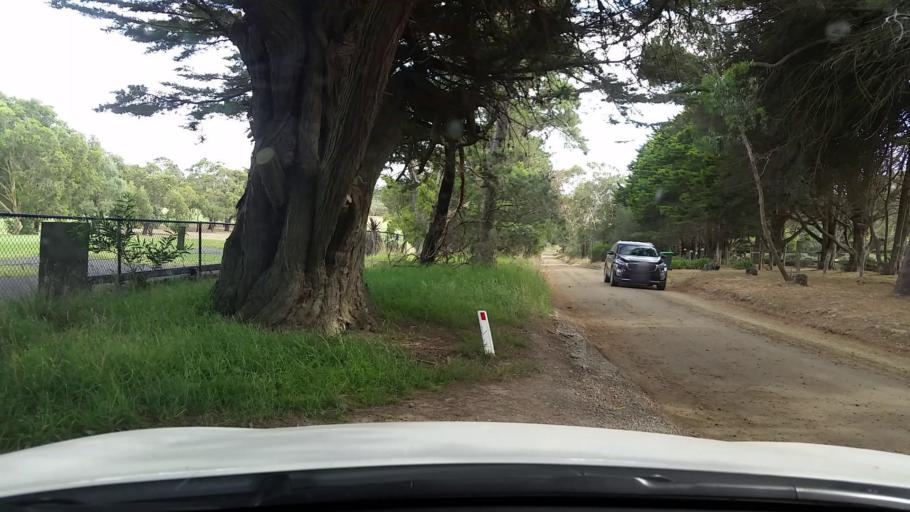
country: AU
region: Victoria
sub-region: Mornington Peninsula
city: Mount Martha
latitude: -38.2848
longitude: 145.0275
